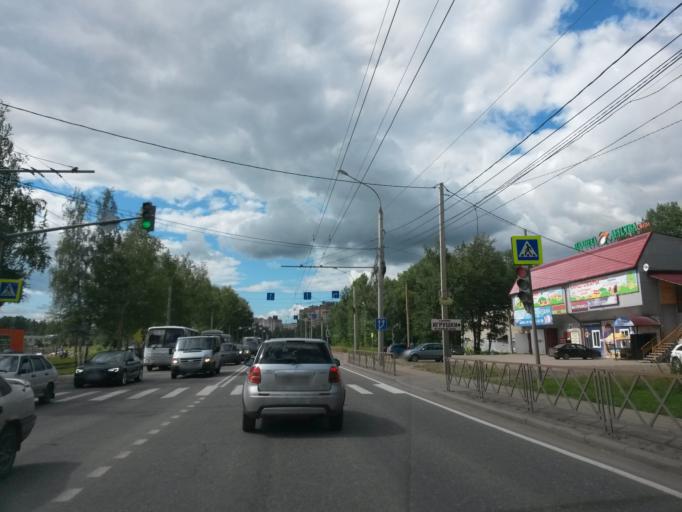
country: RU
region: Jaroslavl
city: Yaroslavl
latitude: 57.6765
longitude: 39.8065
